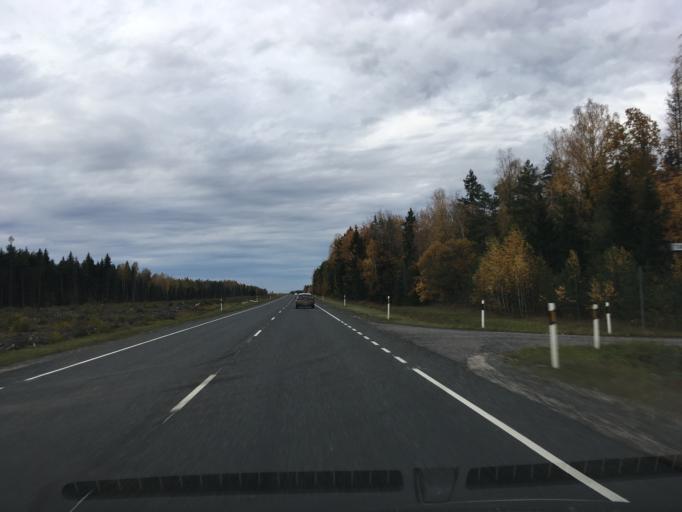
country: EE
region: Harju
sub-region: Nissi vald
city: Turba
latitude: 58.9546
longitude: 24.0791
